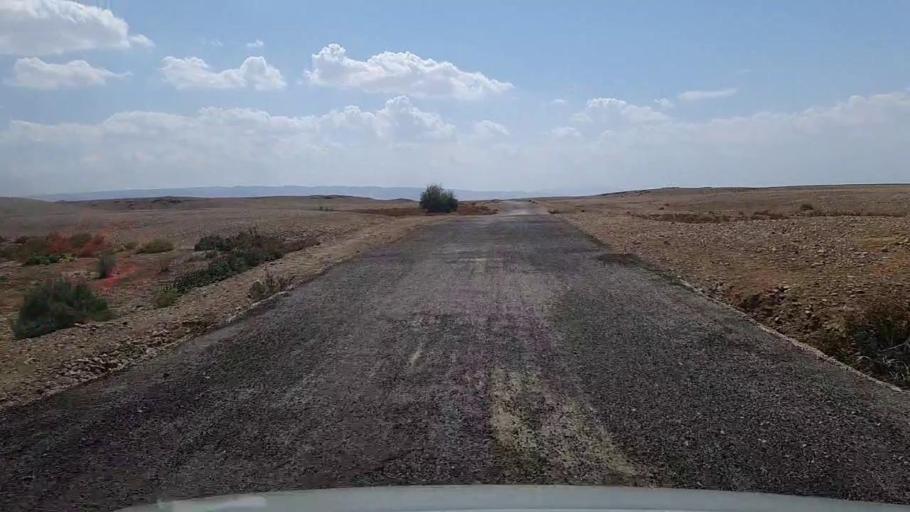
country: PK
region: Sindh
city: Bhan
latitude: 26.3808
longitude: 67.6338
